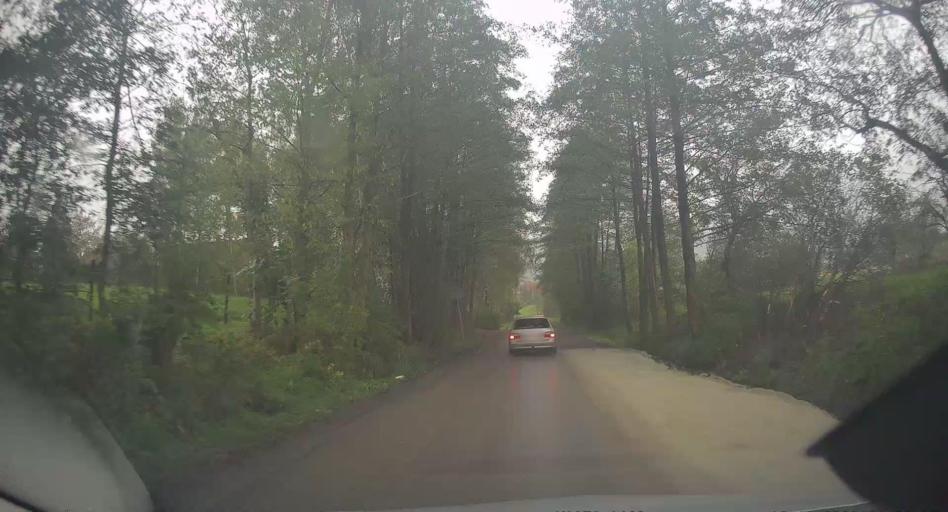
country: PL
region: Lesser Poland Voivodeship
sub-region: Powiat krakowski
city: Ochojno
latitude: 49.9710
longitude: 19.9982
